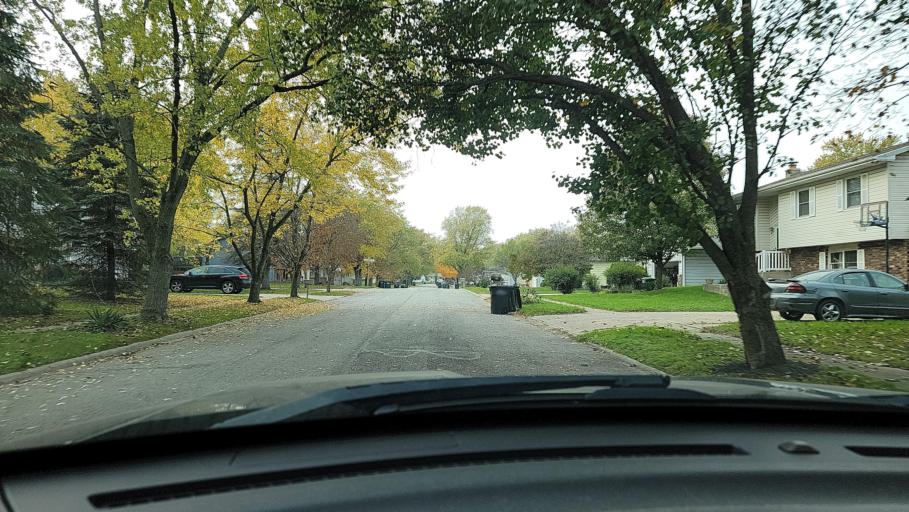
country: US
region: Indiana
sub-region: Porter County
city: Portage
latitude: 41.5916
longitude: -87.1595
